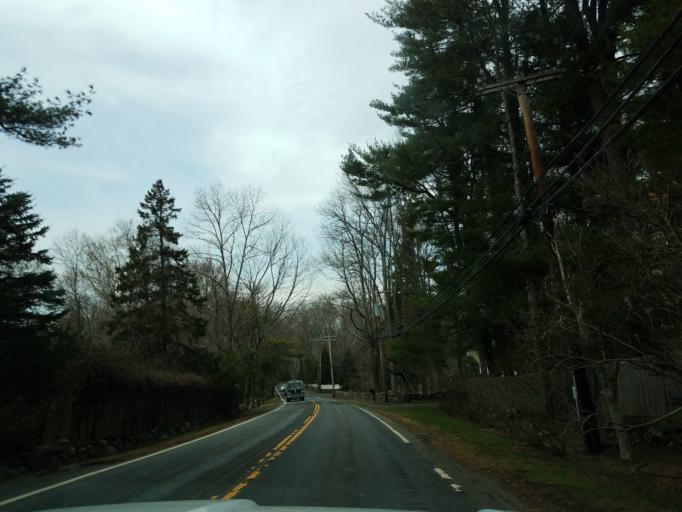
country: US
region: Connecticut
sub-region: Fairfield County
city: Glenville
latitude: 41.0601
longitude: -73.6392
